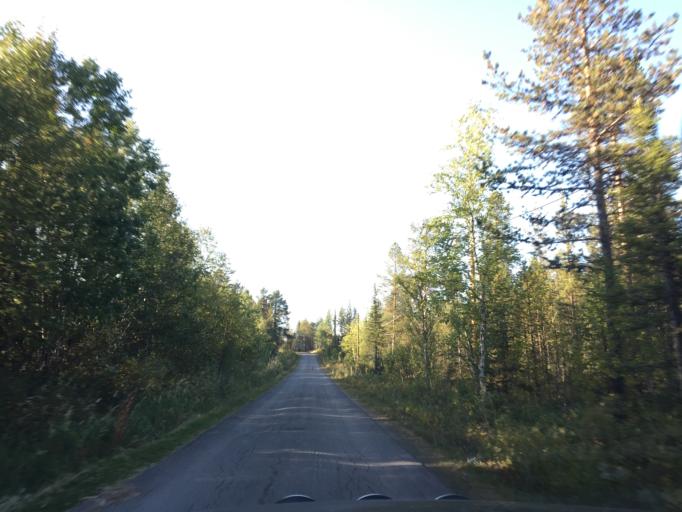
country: SE
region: Norrbotten
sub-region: Gallivare Kommun
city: Malmberget
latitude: 67.6529
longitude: 21.0401
